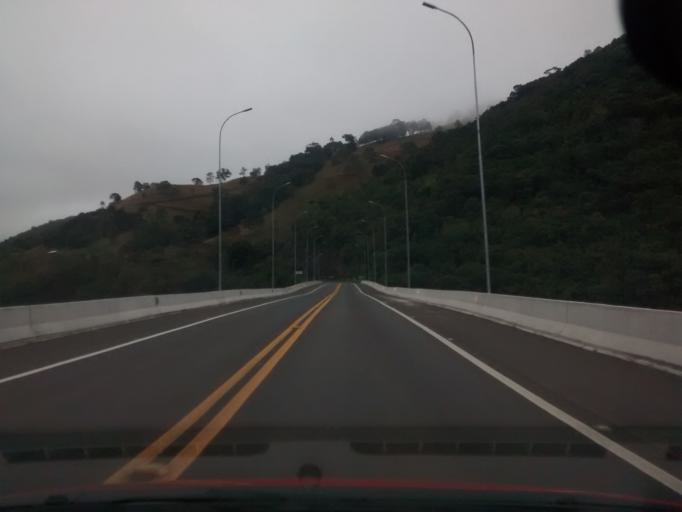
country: BR
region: Rio Grande do Sul
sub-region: Vacaria
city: Estrela
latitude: -28.2099
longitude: -50.7594
